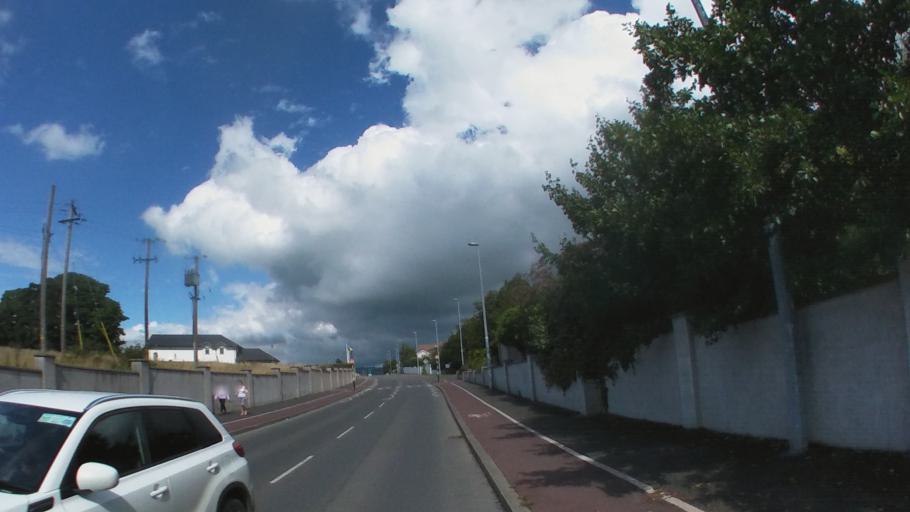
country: IE
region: Leinster
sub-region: Kilkenny
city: Kilkenny
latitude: 52.6671
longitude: -7.2364
